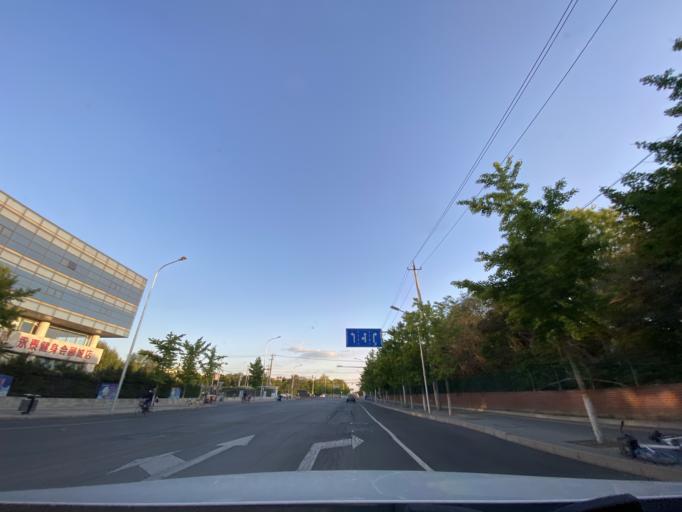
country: CN
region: Beijing
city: Sijiqing
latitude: 39.9469
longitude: 116.2627
